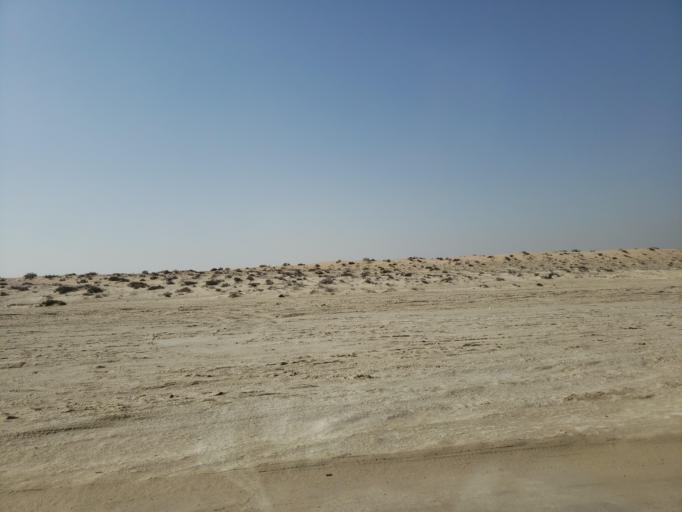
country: AE
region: Umm al Qaywayn
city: Umm al Qaywayn
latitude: 25.5321
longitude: 55.6043
